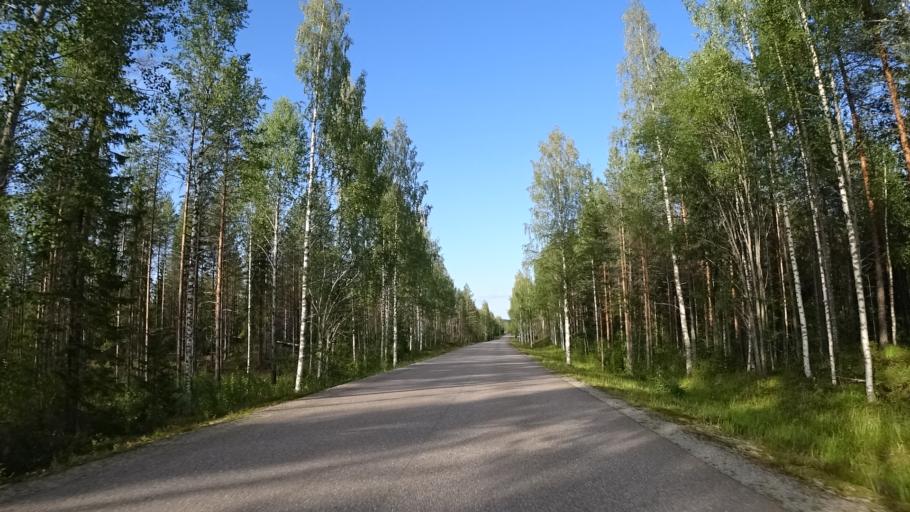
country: FI
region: North Karelia
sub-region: Joensuu
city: Eno
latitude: 63.0110
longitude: 30.4762
